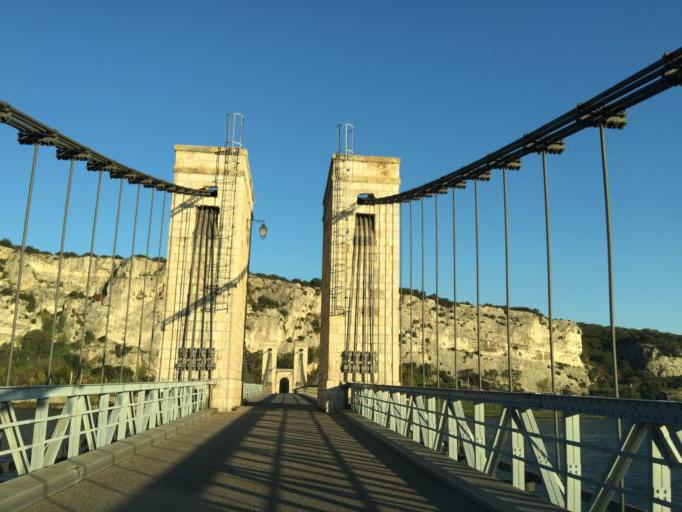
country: FR
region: Rhone-Alpes
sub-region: Departement de la Drome
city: Donzere
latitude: 44.4525
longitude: 4.6971
